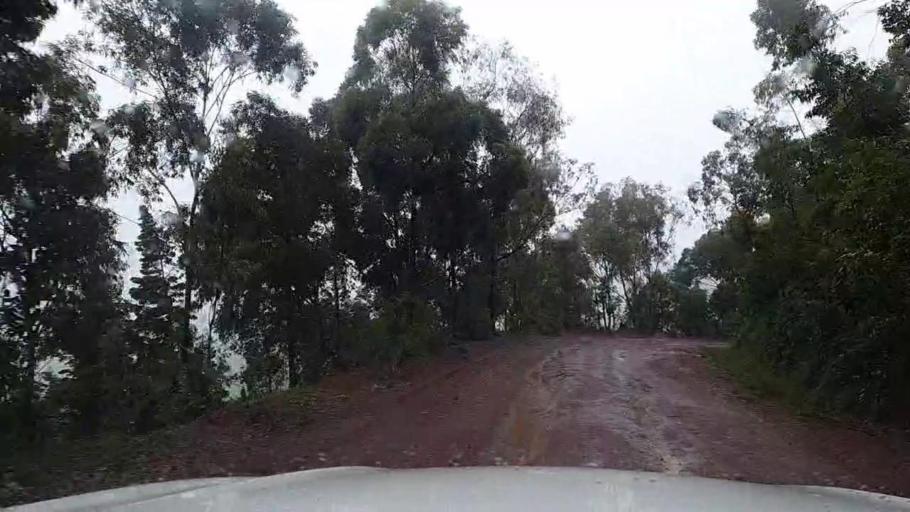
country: RW
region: Kigali
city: Kigali
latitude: -1.7649
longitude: 29.9932
